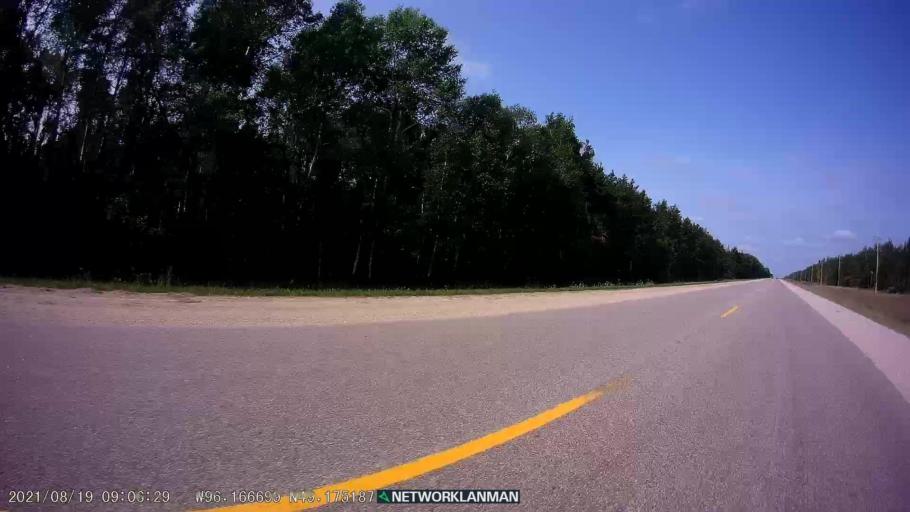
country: CA
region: Manitoba
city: La Broquerie
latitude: 49.1753
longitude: -96.1676
